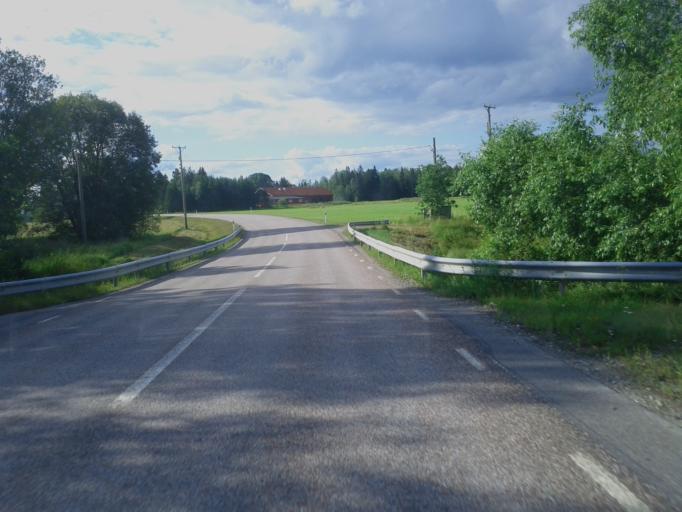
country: SE
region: Vaestmanland
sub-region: Sala Kommun
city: Sala
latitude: 59.9141
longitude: 16.5185
